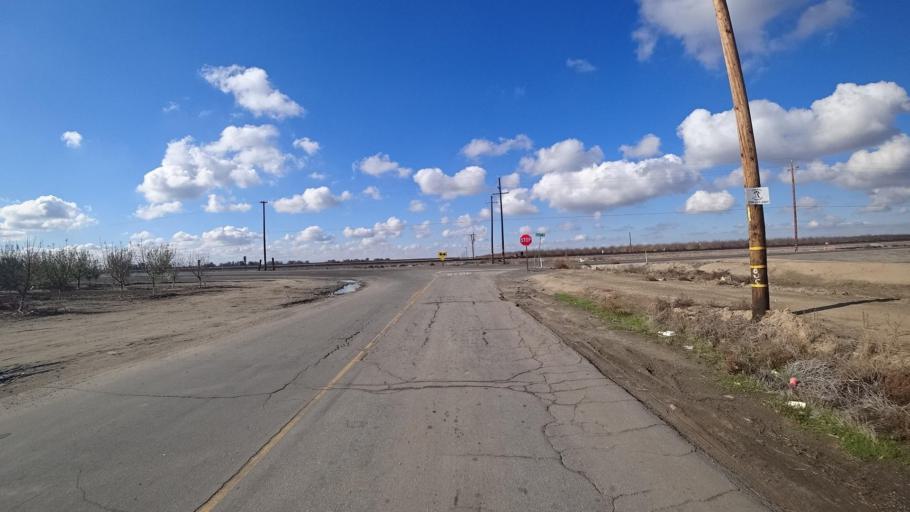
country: US
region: California
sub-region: Kern County
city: Wasco
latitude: 35.6742
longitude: -119.3300
